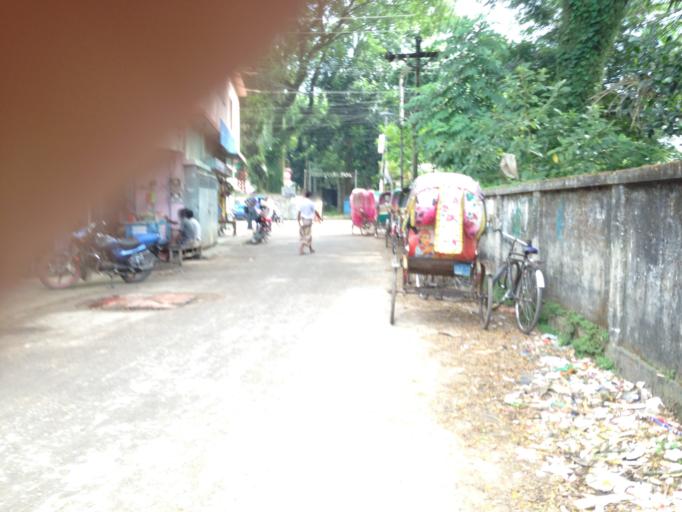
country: IN
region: Tripura
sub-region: Dhalai
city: Kamalpur
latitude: 24.3090
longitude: 91.7273
